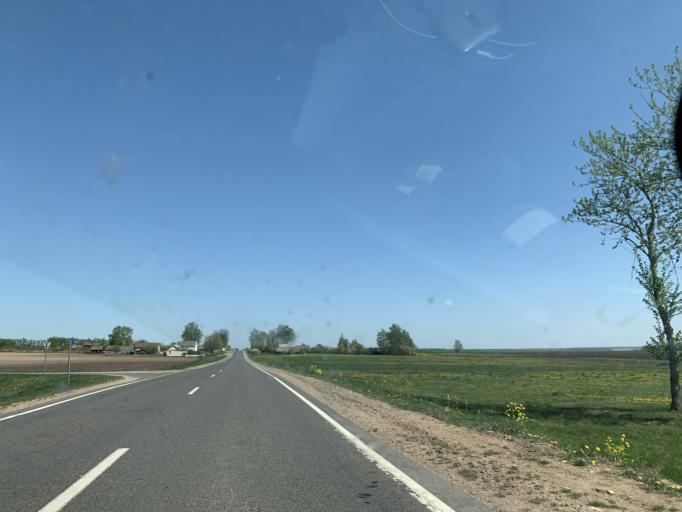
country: BY
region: Minsk
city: Nyasvizh
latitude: 53.2352
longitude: 26.8174
